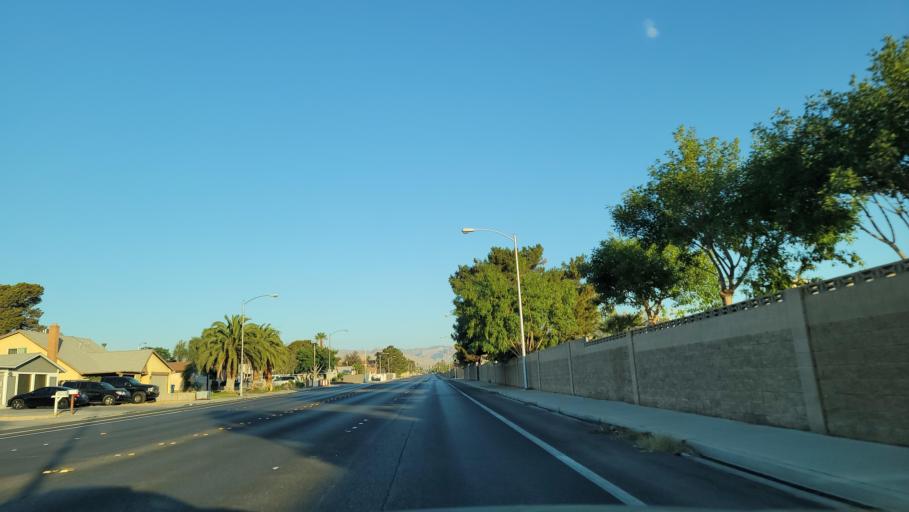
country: US
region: Nevada
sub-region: Clark County
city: Spring Valley
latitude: 36.1219
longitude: -115.2323
